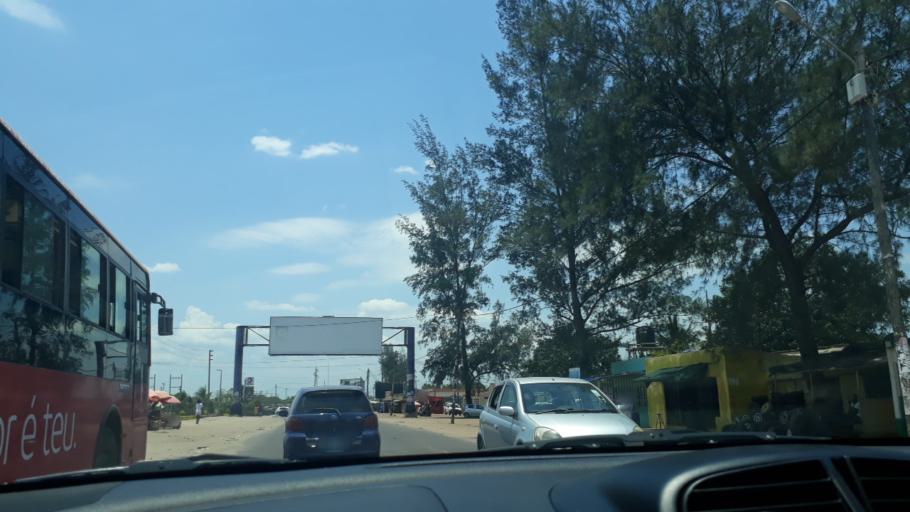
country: MZ
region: Maputo City
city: Maputo
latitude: -25.8870
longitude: 32.6039
